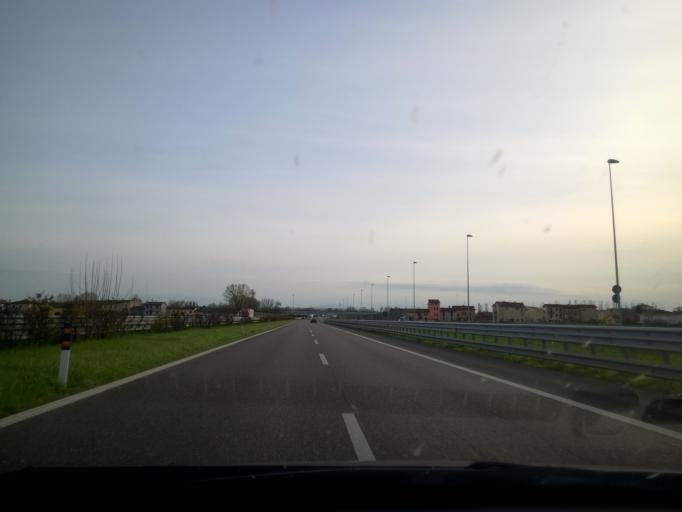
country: IT
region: Lombardy
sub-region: Provincia di Cremona
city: Battaglione-Bagnara
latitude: 45.1212
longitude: 10.0618
